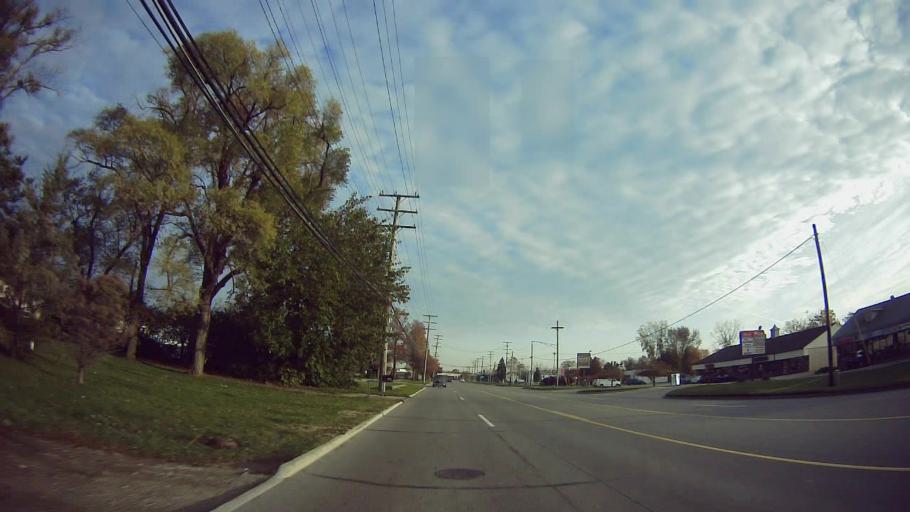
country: US
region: Michigan
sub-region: Macomb County
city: Mount Clemens
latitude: 42.5493
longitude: -82.8748
